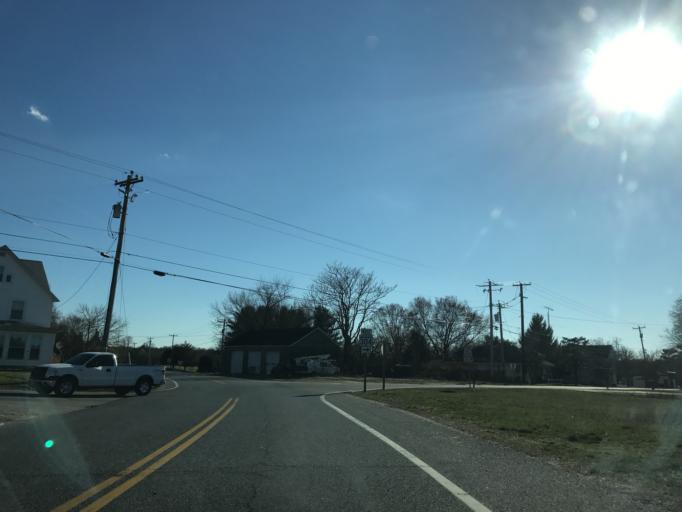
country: US
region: Maryland
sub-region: Caroline County
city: Ridgely
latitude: 39.0350
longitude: -75.8743
